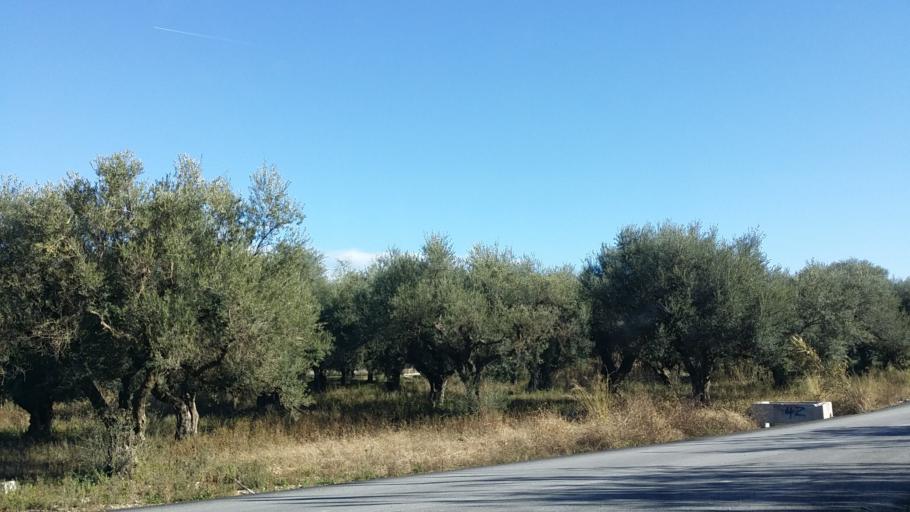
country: GR
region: West Greece
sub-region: Nomos Achaias
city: Temeni
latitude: 38.1929
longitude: 22.1850
